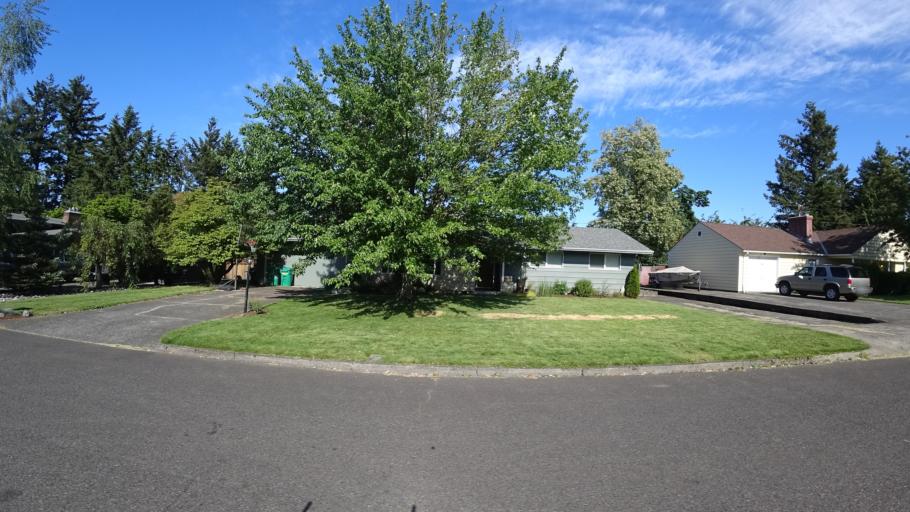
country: US
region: Oregon
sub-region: Multnomah County
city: Fairview
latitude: 45.5290
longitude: -122.5052
